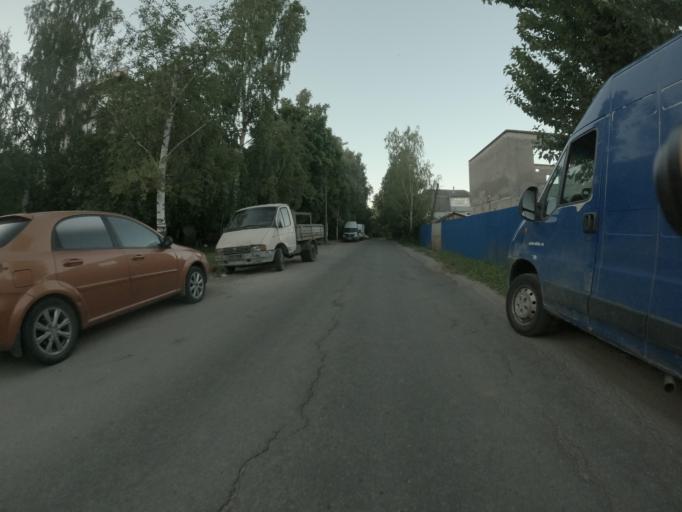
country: RU
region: St.-Petersburg
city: Krasnogvargeisky
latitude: 59.9763
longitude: 30.5124
